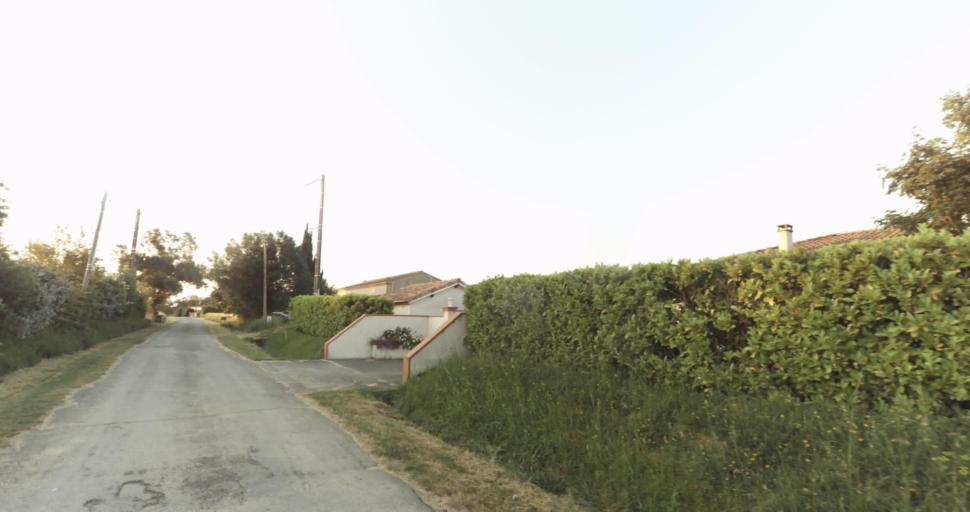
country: FR
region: Midi-Pyrenees
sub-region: Departement du Gers
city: Pujaudran
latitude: 43.6539
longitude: 1.0966
